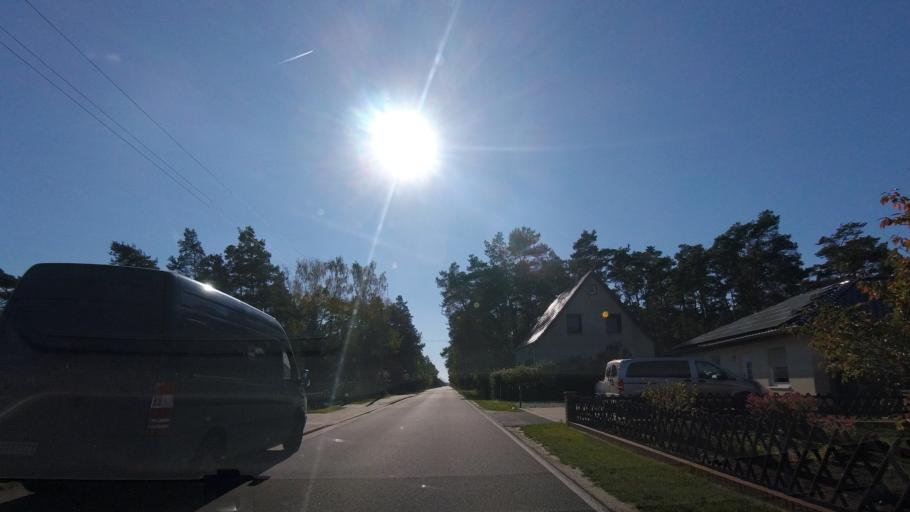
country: DE
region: Saxony-Anhalt
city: Muhlanger
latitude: 51.8561
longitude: 12.7733
